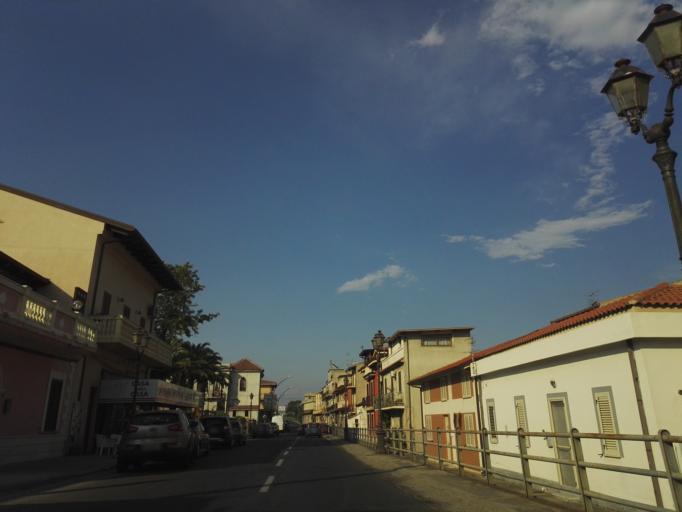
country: IT
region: Calabria
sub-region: Provincia di Reggio Calabria
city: Siderno
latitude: 38.2734
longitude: 16.3038
